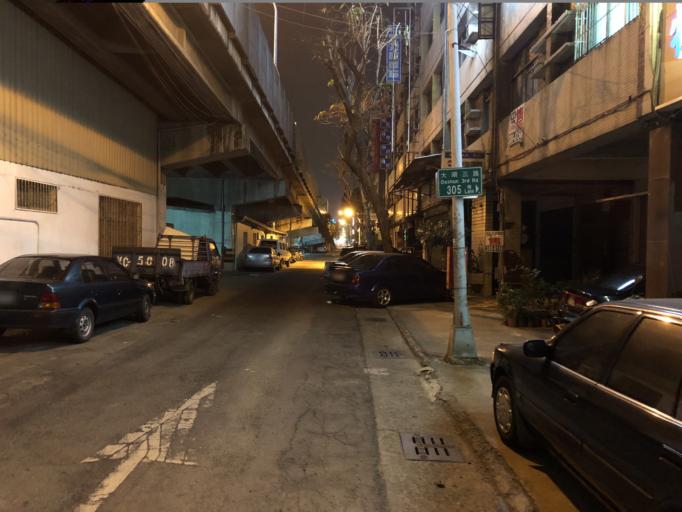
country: TW
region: Kaohsiung
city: Kaohsiung
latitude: 22.6367
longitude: 120.3270
